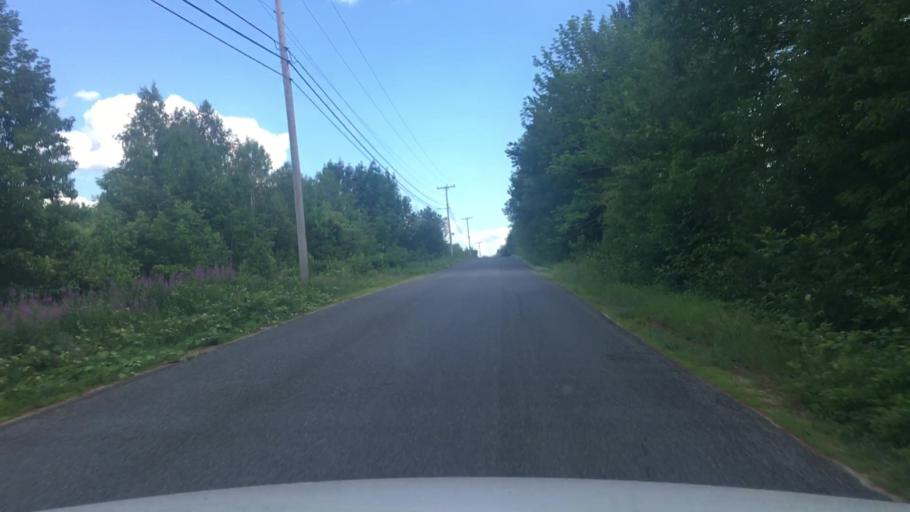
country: US
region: Maine
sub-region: Franklin County
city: Wilton
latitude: 44.6127
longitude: -70.2332
